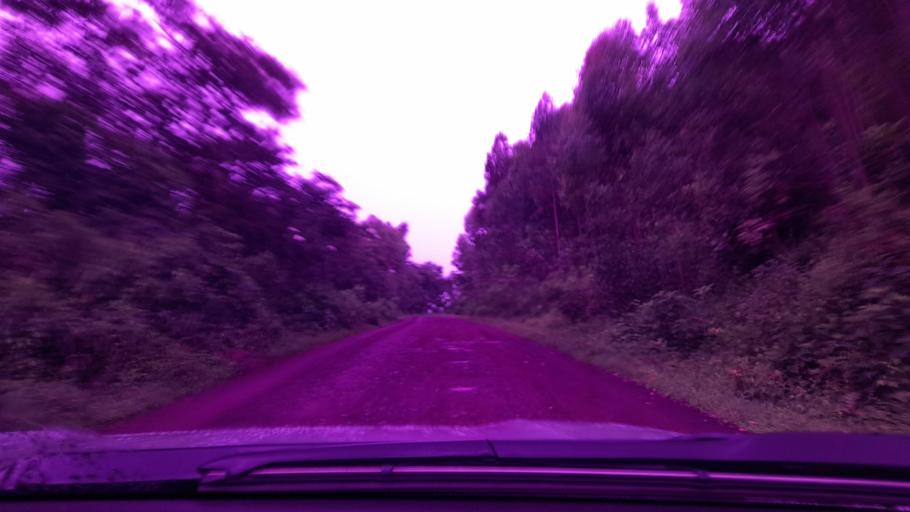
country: ET
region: Oromiya
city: Metu
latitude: 8.4496
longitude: 35.6310
